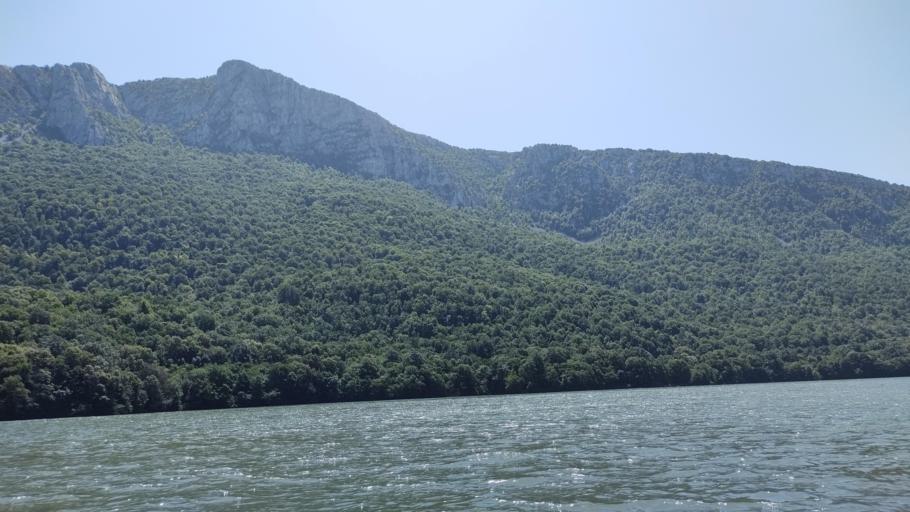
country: RO
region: Mehedinti
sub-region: Comuna Dubova
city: Dubova
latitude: 44.5998
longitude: 22.2653
